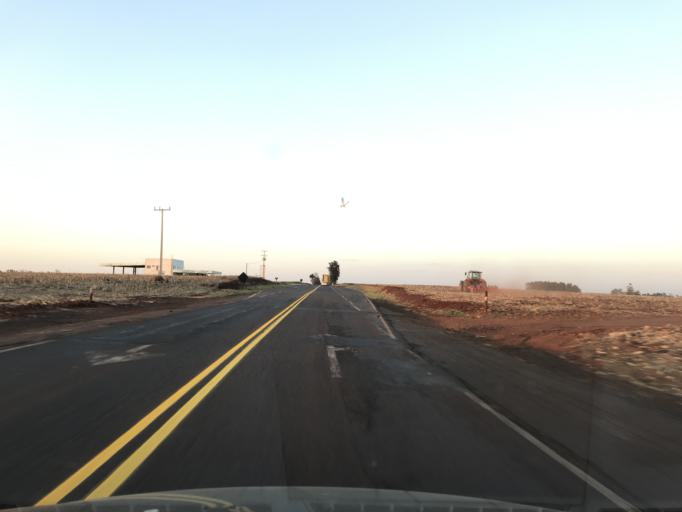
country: BR
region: Parana
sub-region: Palotina
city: Palotina
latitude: -24.4071
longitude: -53.8630
